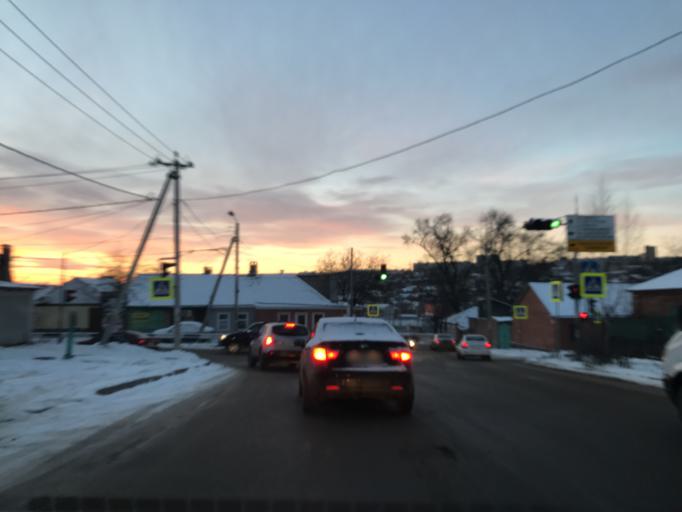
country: RU
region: Rostov
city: Rostov-na-Donu
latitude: 47.2270
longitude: 39.6817
